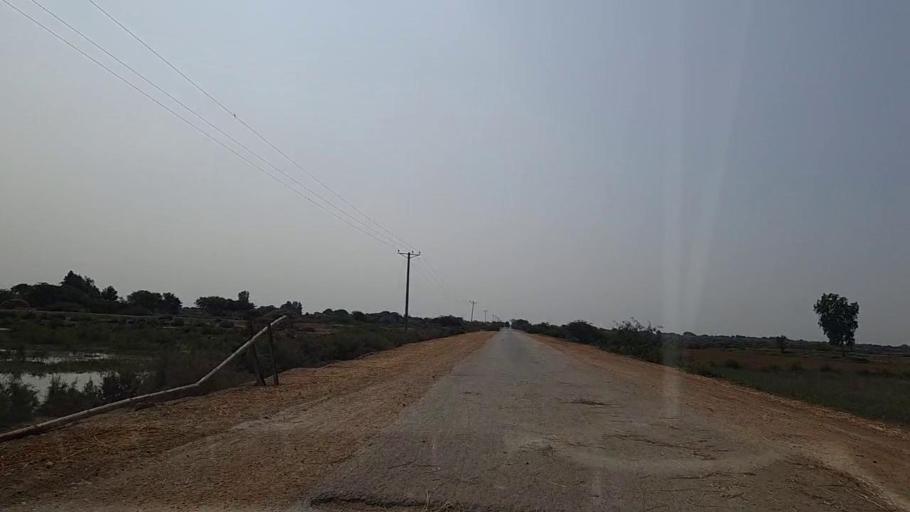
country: PK
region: Sindh
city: Chuhar Jamali
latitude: 24.2824
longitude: 67.9206
